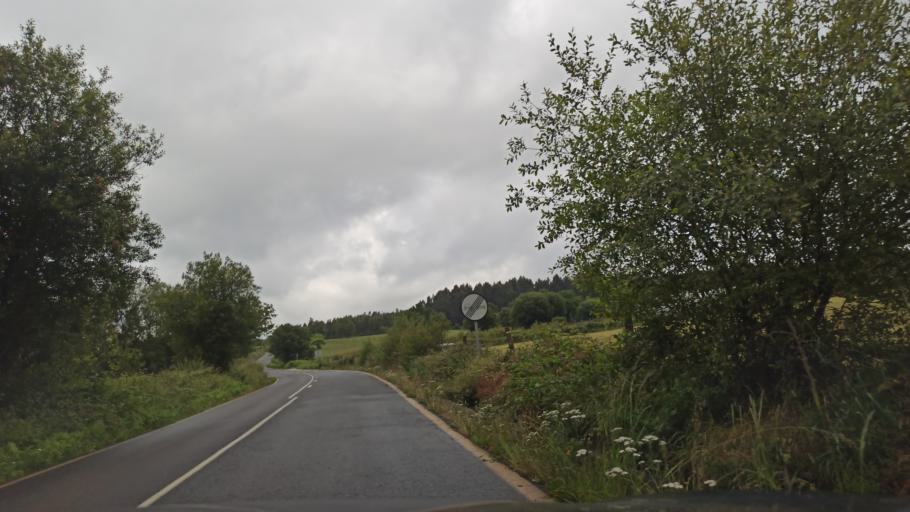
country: ES
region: Galicia
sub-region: Provincia da Coruna
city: Santiso
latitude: 42.7708
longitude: -8.0291
